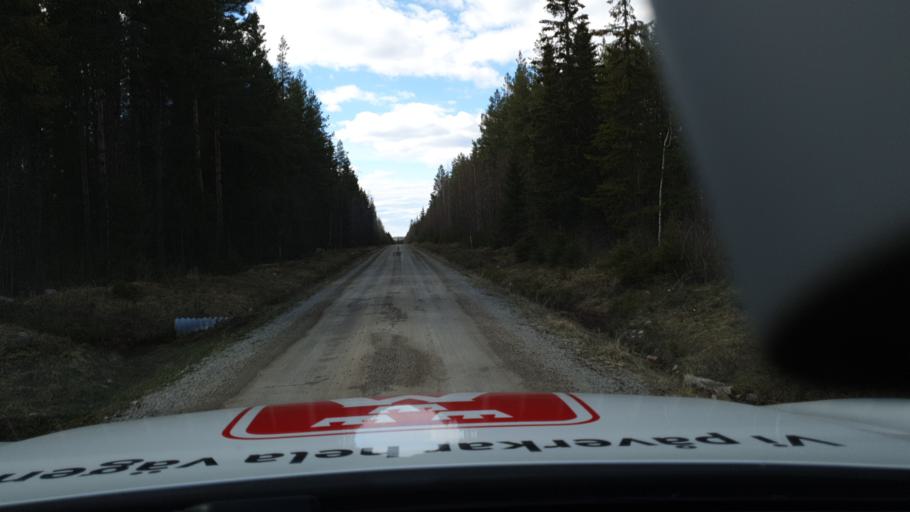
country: SE
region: Jaemtland
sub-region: Bergs Kommun
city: Hoverberg
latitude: 62.8003
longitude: 14.6720
